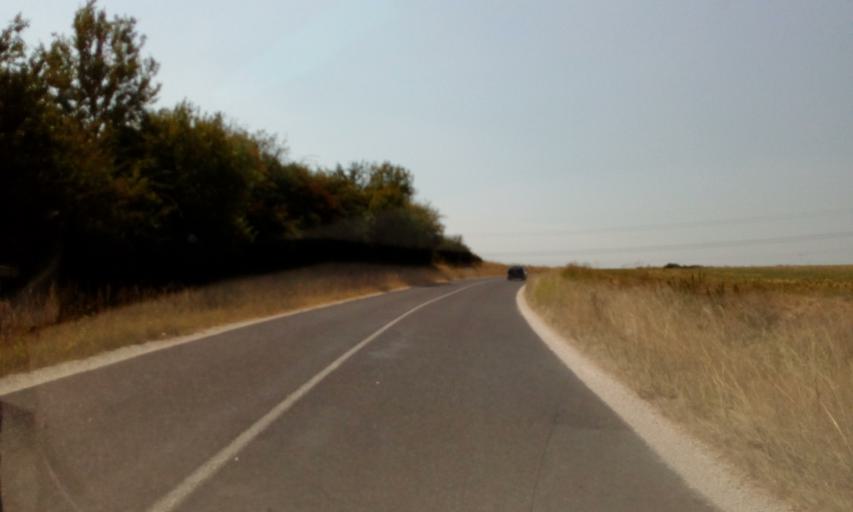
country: FR
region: Lorraine
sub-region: Departement de la Meuse
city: Montmedy
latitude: 49.4414
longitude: 5.3870
